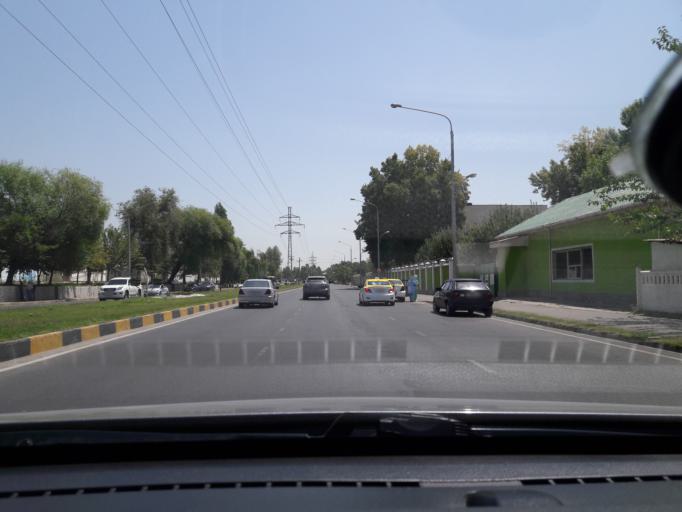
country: TJ
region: Dushanbe
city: Dushanbe
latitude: 38.5936
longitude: 68.7467
